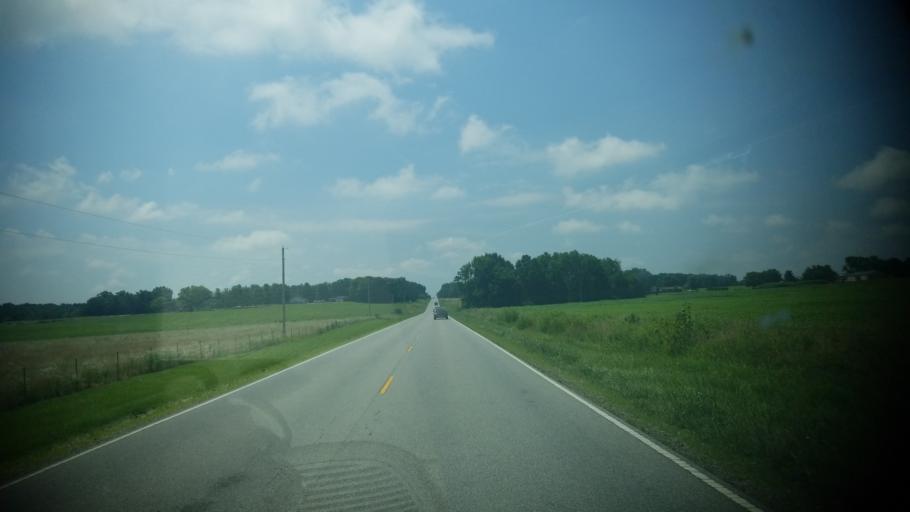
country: US
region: Illinois
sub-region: Wayne County
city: Fairfield
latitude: 38.4206
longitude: -88.3499
